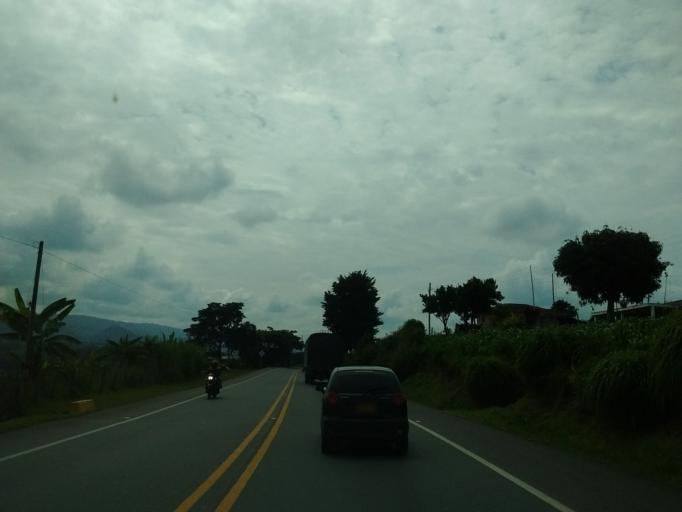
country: CO
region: Cauca
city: Morales
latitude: 2.7661
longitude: -76.5534
